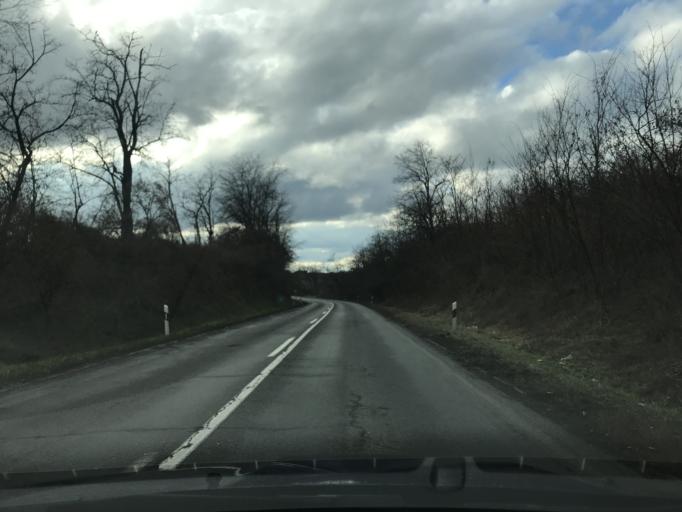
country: HU
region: Bacs-Kiskun
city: Nemesnadudvar
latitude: 46.3396
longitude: 19.0685
